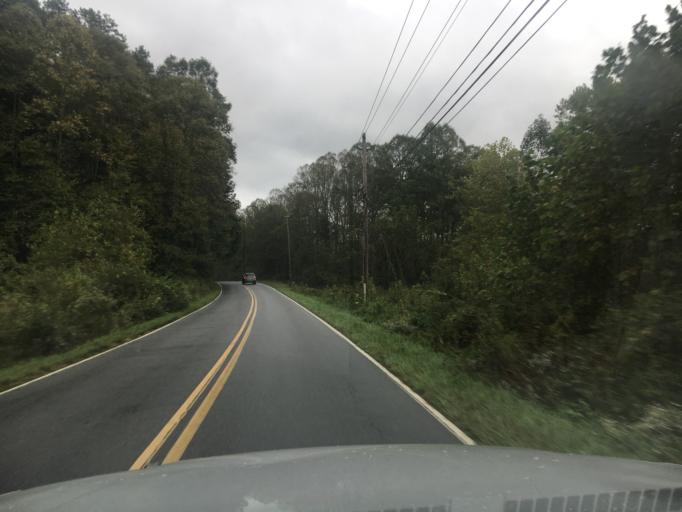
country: US
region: North Carolina
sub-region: Transylvania County
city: Brevard
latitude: 35.2541
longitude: -82.6921
